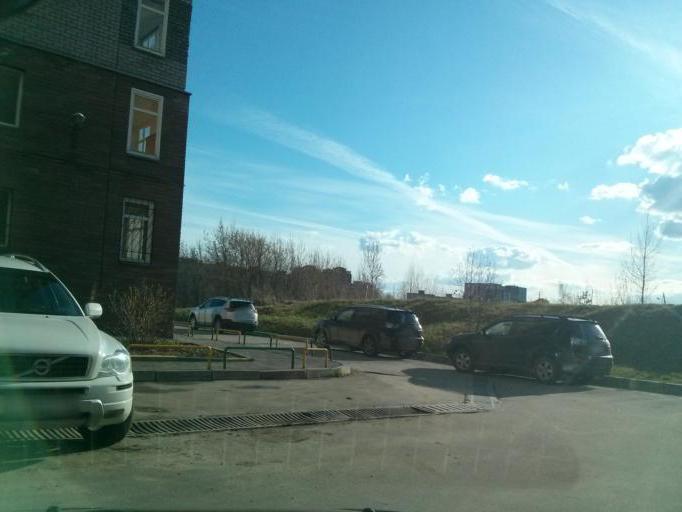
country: RU
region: Nizjnij Novgorod
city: Afonino
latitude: 56.3023
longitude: 44.0699
